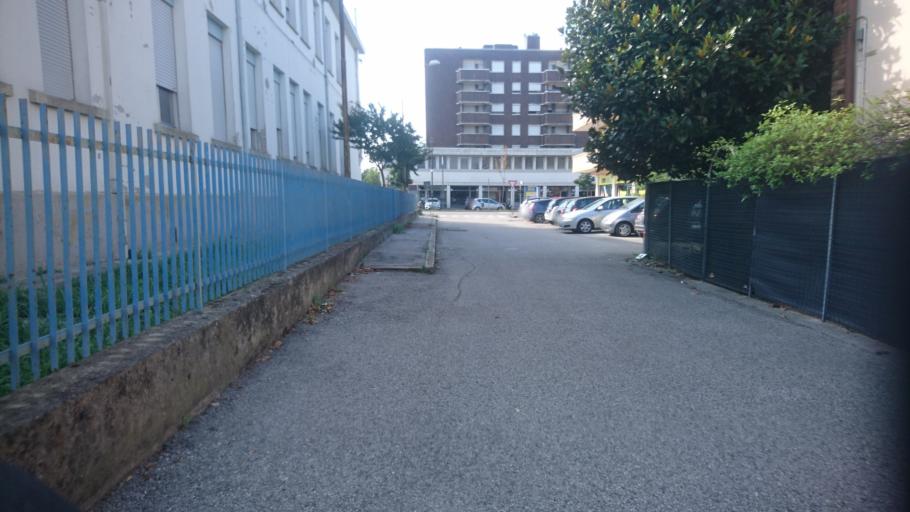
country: IT
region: Veneto
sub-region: Provincia di Padova
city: Tencarola
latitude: 45.3921
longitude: 11.8110
